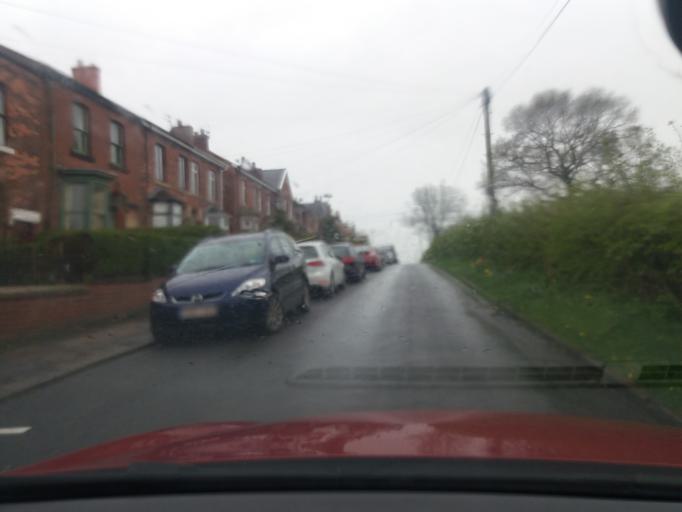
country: GB
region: England
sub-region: Lancashire
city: Chorley
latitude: 53.6859
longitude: -2.6076
